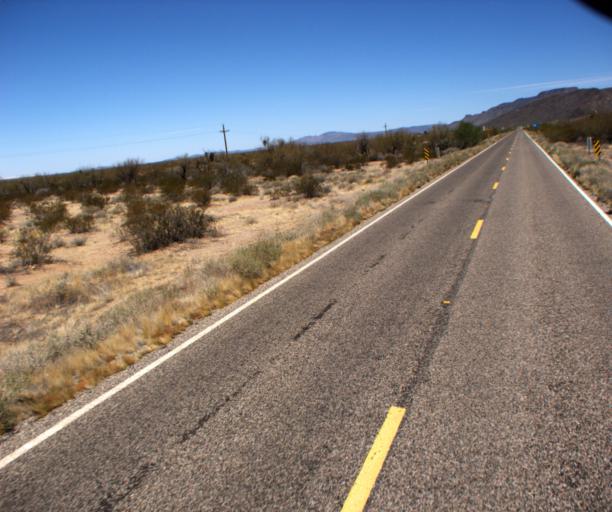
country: US
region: Arizona
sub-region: Pima County
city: Ajo
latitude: 32.2480
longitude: -112.7467
